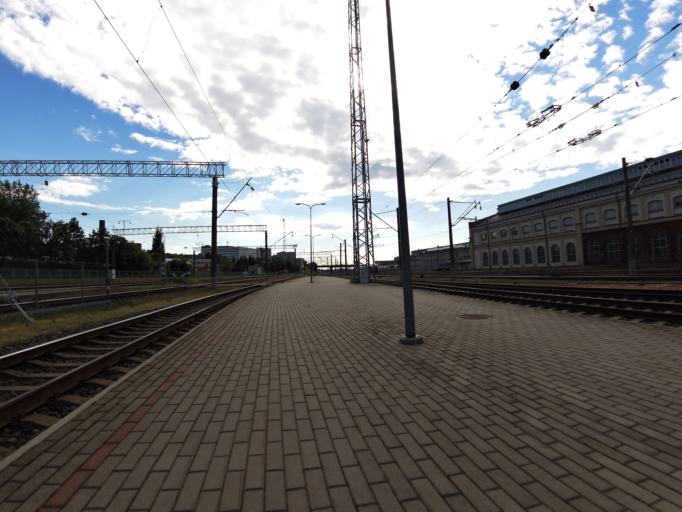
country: LT
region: Vilnius County
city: Naujamiestis
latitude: 54.6678
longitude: 25.2800
